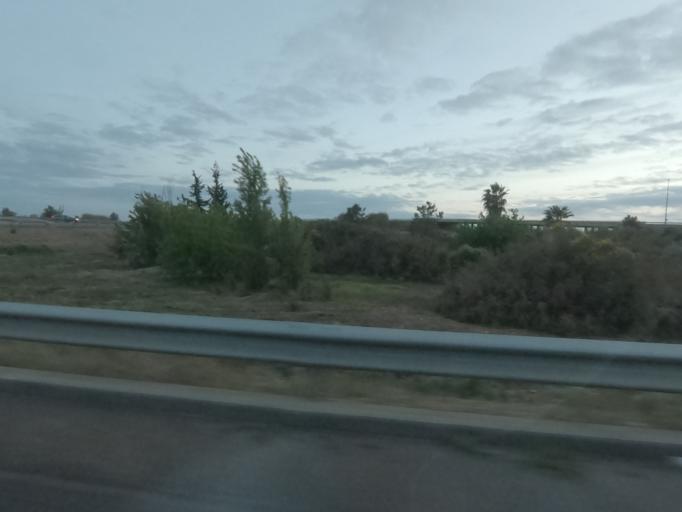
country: ES
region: Extremadura
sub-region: Provincia de Badajoz
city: Badajoz
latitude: 38.9214
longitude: -6.9634
